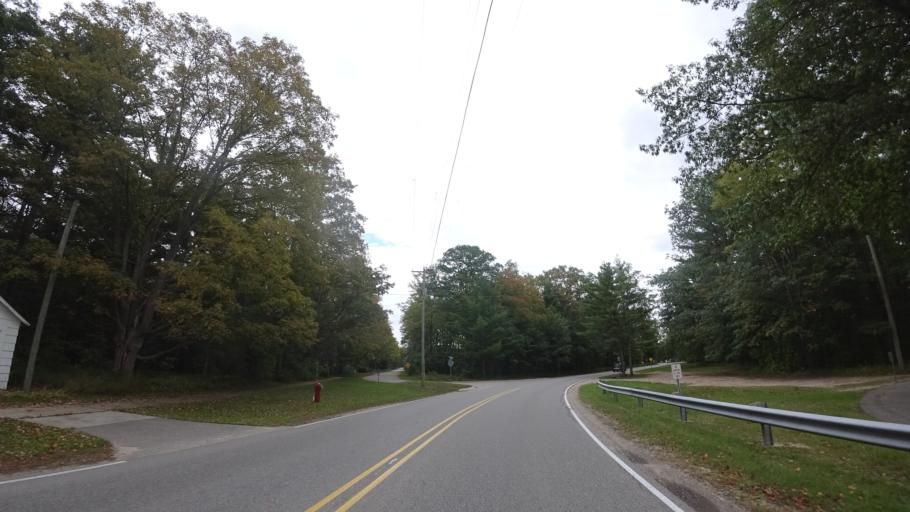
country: US
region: Michigan
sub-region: Emmet County
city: Harbor Springs
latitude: 45.4353
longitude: -84.9733
